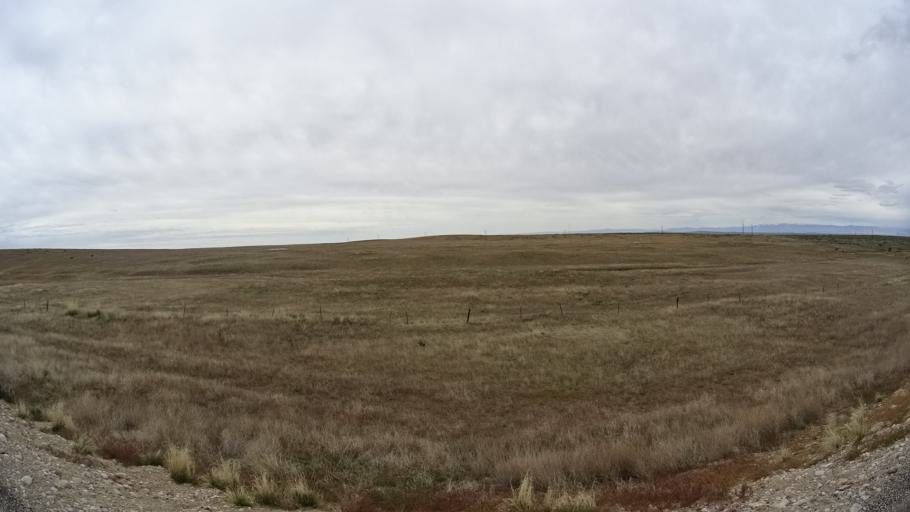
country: US
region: Idaho
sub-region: Ada County
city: Boise
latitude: 43.4691
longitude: -116.0664
